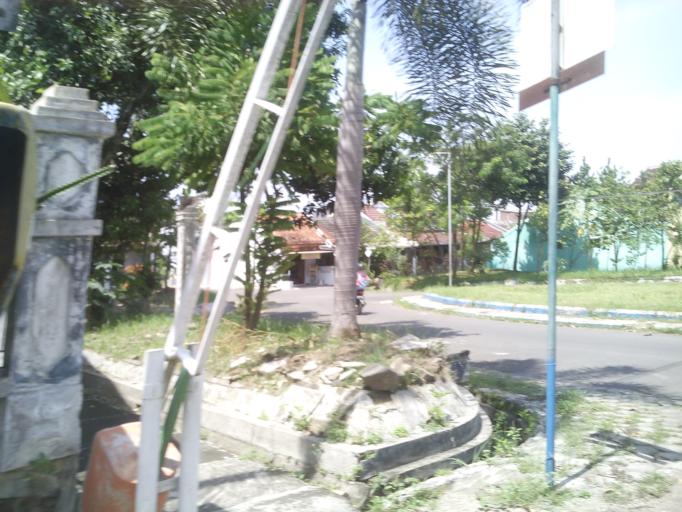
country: ID
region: East Java
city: Sumbersari Wetan
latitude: -8.1766
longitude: 113.7203
